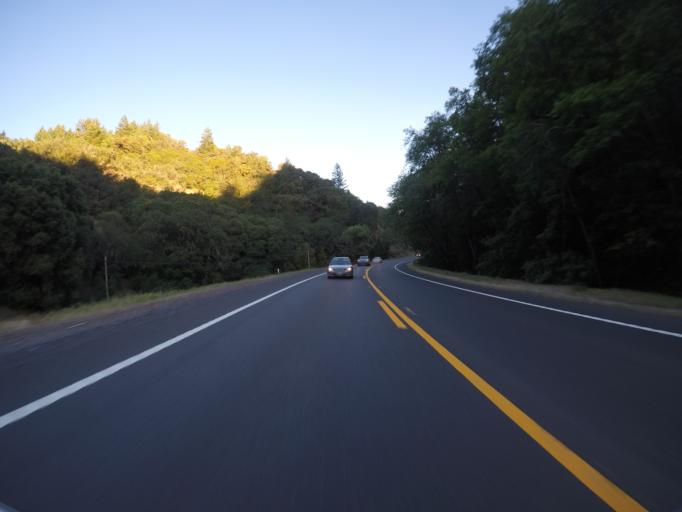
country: US
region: California
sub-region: Mendocino County
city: Laytonville
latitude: 39.8224
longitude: -123.5649
